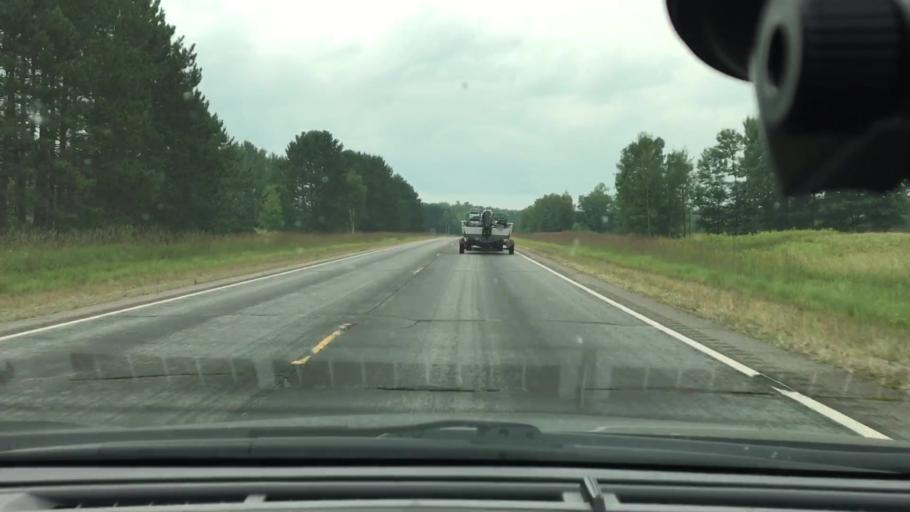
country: US
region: Minnesota
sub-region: Crow Wing County
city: Crosby
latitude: 46.6344
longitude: -93.9482
